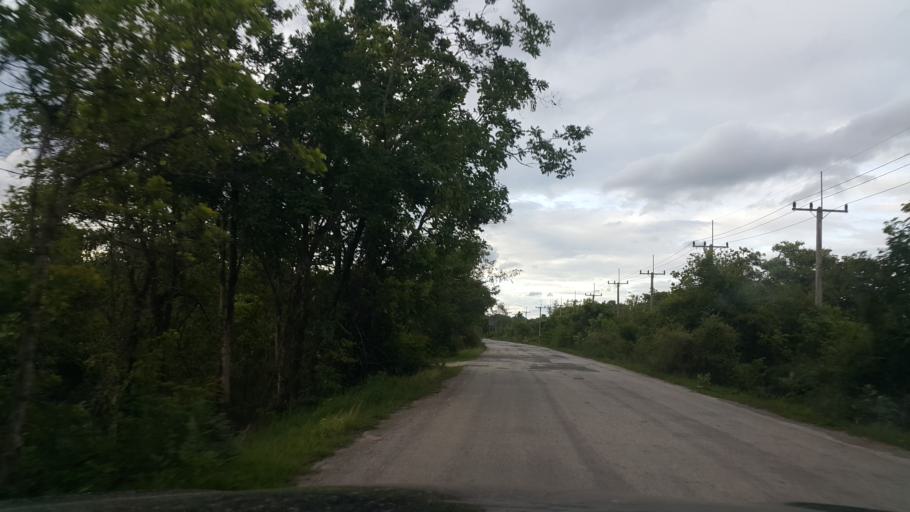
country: TH
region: Sukhothai
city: Thung Saliam
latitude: 17.1730
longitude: 99.5248
